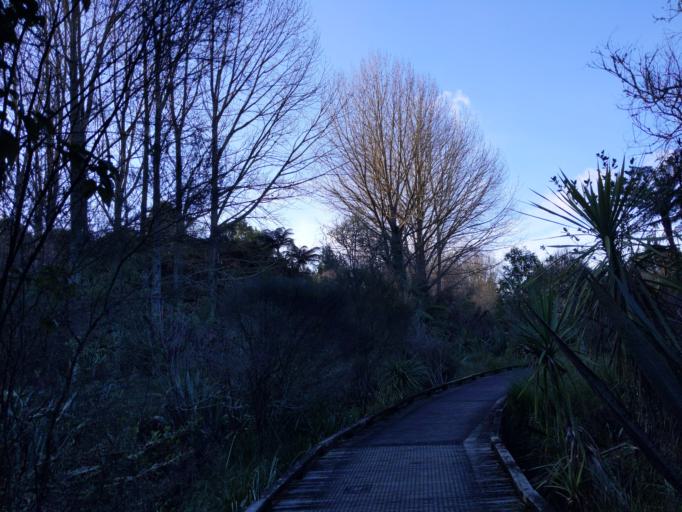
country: NZ
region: Waikato
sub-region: Hamilton City
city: Hamilton
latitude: -37.7407
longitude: 175.2752
